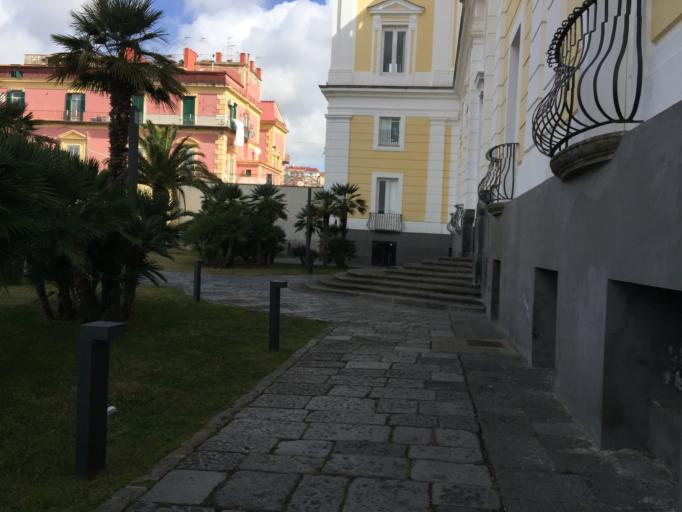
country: IT
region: Campania
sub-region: Provincia di Napoli
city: Ercolano
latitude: 40.8015
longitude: 14.3529
